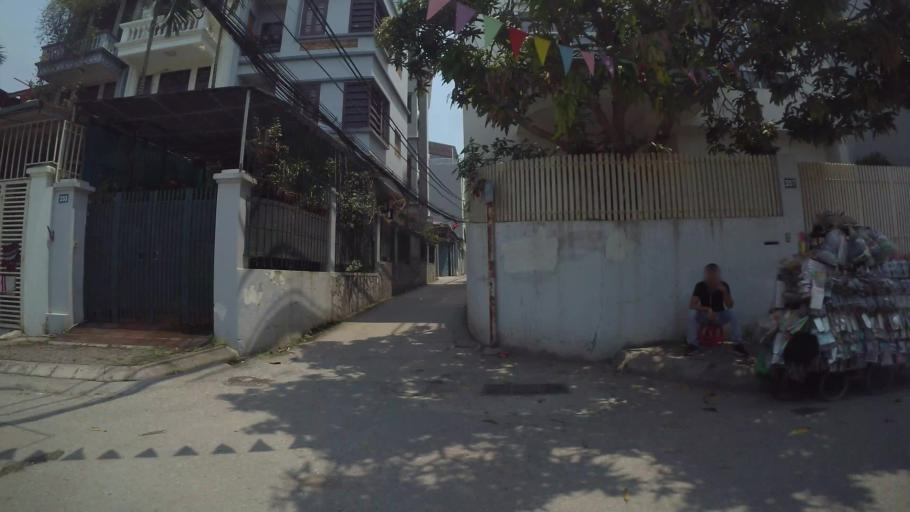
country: VN
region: Ha Noi
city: Hoan Kiem
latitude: 21.0343
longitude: 105.8773
